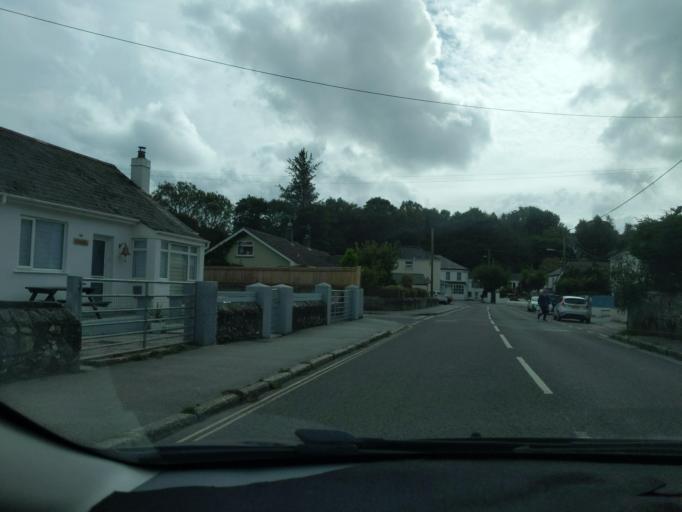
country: GB
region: England
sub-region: Cornwall
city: Par
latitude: 50.3516
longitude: -4.7107
